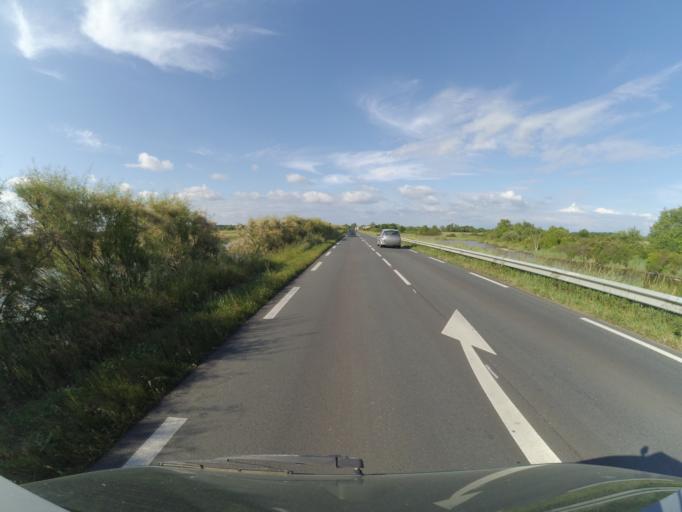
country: FR
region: Poitou-Charentes
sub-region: Departement de la Charente-Maritime
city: Le Gua
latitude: 45.7206
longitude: -0.9673
